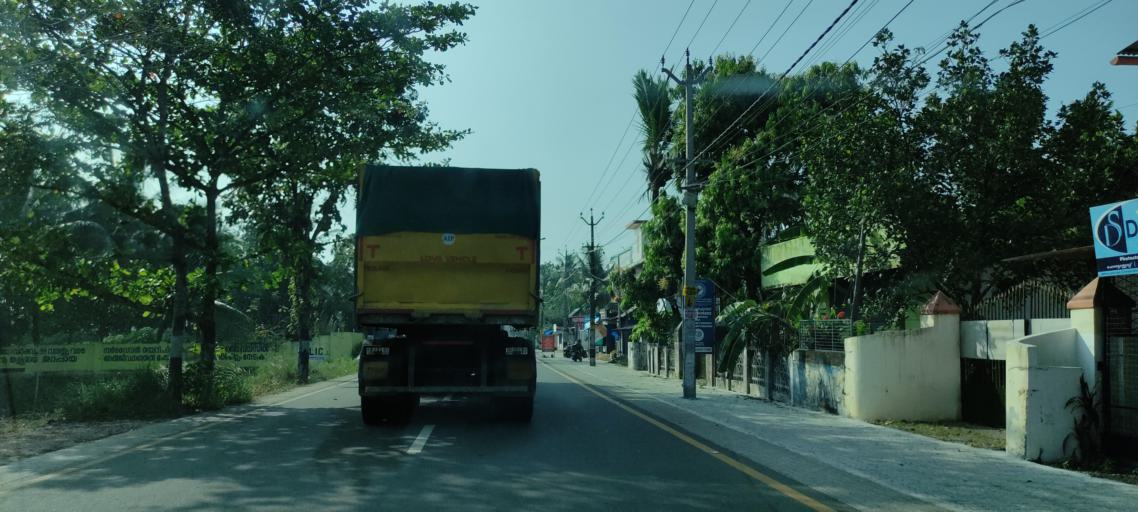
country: IN
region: Kerala
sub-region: Kottayam
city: Changanacheri
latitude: 9.3619
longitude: 76.4592
